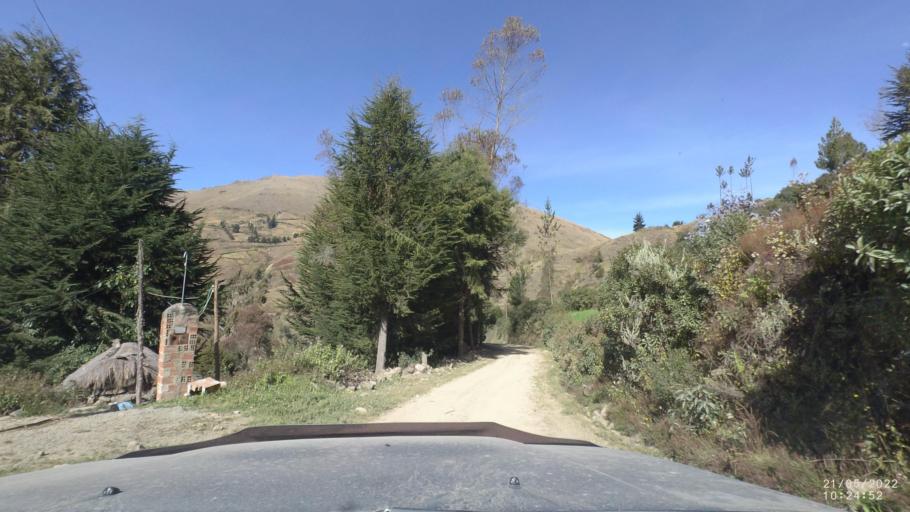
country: BO
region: Cochabamba
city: Colomi
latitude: -17.3246
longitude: -65.9487
